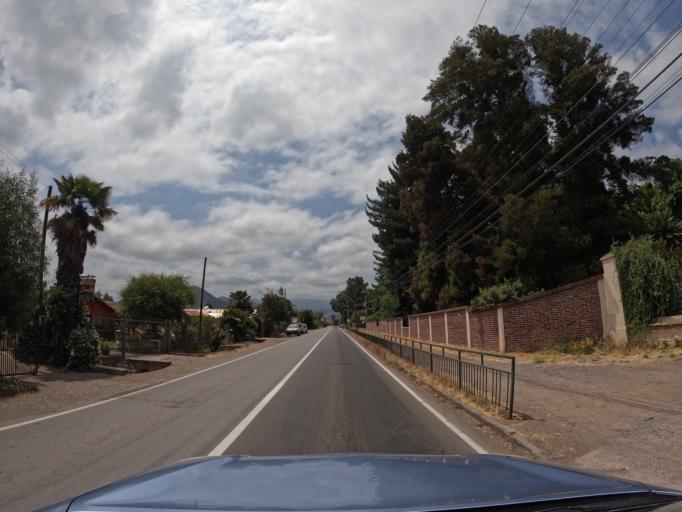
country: CL
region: O'Higgins
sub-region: Provincia de Colchagua
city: Chimbarongo
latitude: -34.7346
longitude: -70.9785
